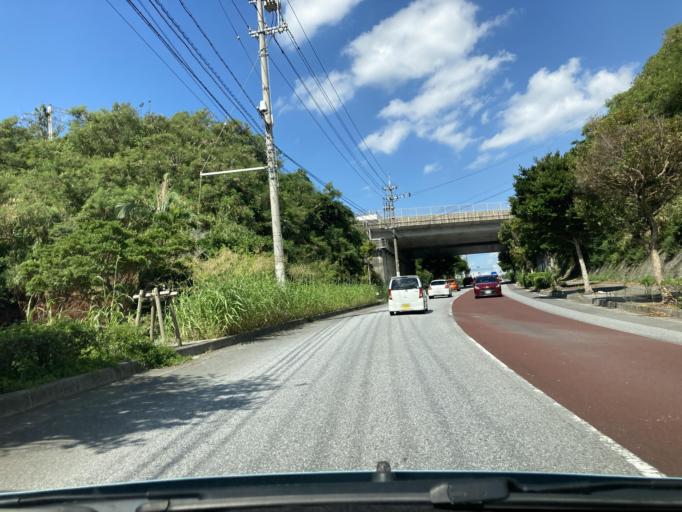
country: JP
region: Okinawa
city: Ginowan
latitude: 26.2485
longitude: 127.7573
